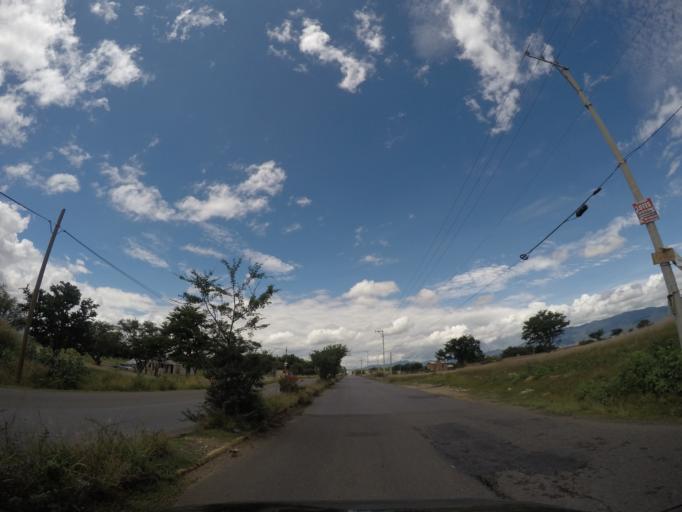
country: MX
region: Oaxaca
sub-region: Santa Cruz Xoxocotlan
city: San Isidro Monjas
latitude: 16.9881
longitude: -96.7456
